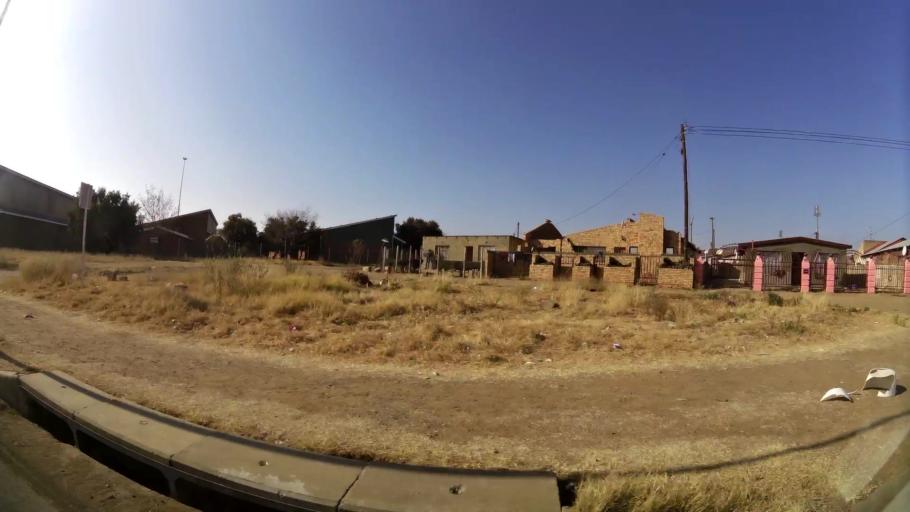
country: ZA
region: Orange Free State
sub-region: Mangaung Metropolitan Municipality
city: Bloemfontein
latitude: -29.1708
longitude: 26.2326
